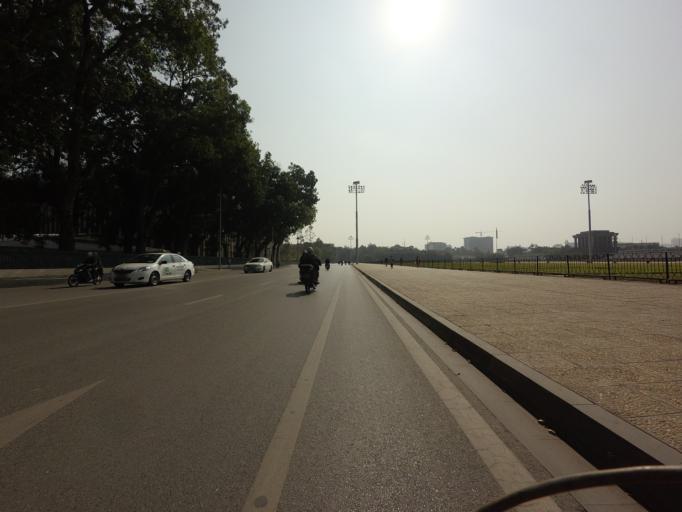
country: VN
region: Ha Noi
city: Hanoi
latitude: 21.0384
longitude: 105.8368
